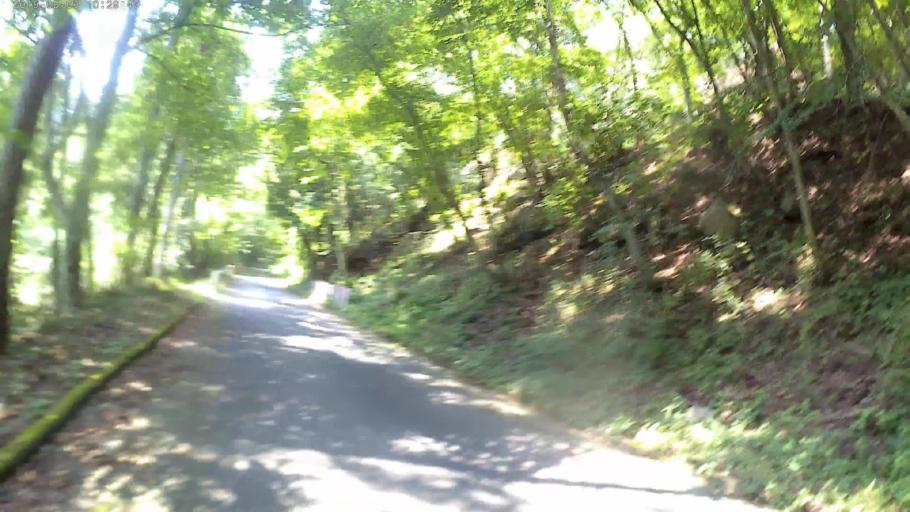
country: JP
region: Yamanashi
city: Enzan
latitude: 35.6270
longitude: 138.7693
